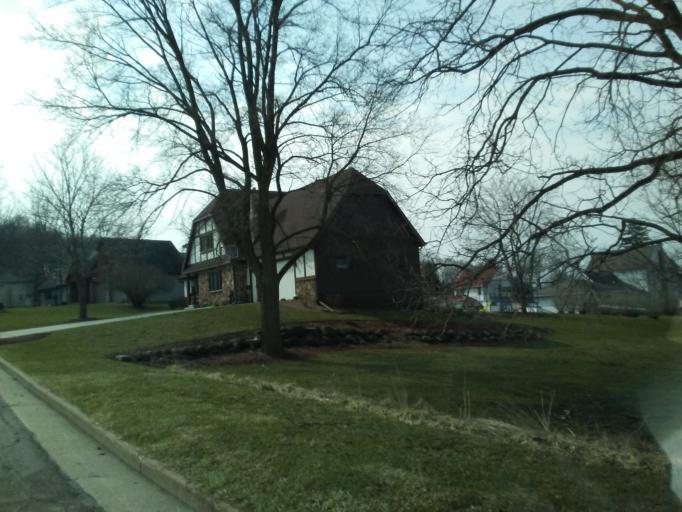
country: US
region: Wisconsin
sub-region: Columbia County
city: Lodi
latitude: 43.3086
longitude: -89.5232
